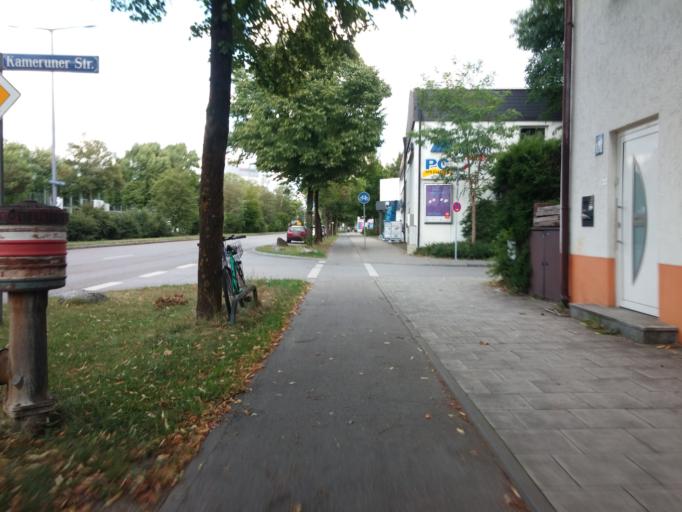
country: DE
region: Bavaria
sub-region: Upper Bavaria
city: Haar
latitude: 48.1109
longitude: 11.7124
